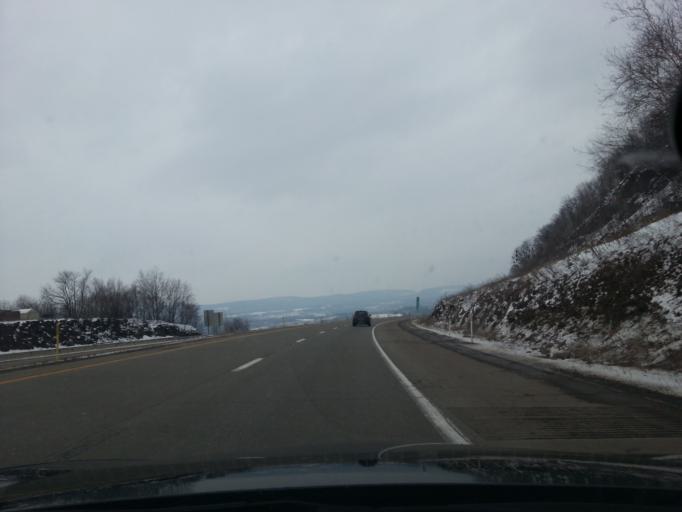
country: US
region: Pennsylvania
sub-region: Luzerne County
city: Conyngham
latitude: 40.9826
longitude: -76.0353
